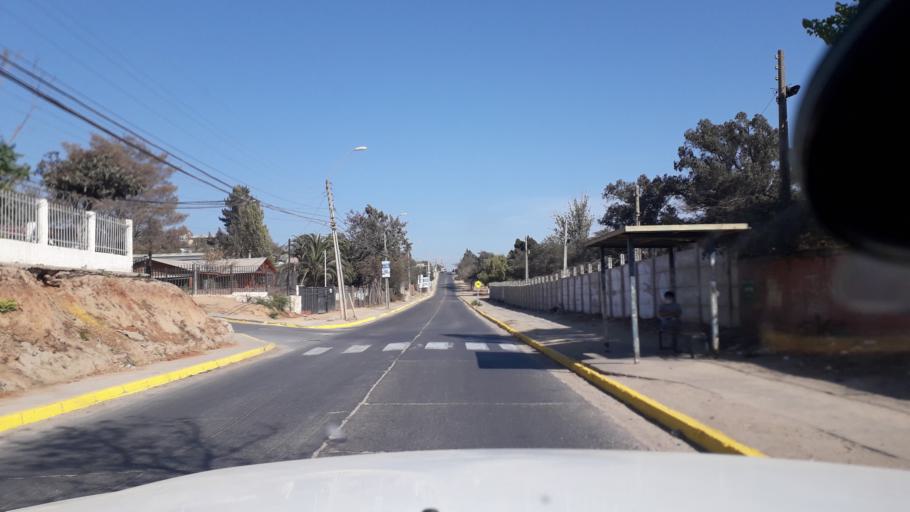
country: CL
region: Valparaiso
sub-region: Provincia de Marga Marga
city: Villa Alemana
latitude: -33.0612
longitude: -71.4024
